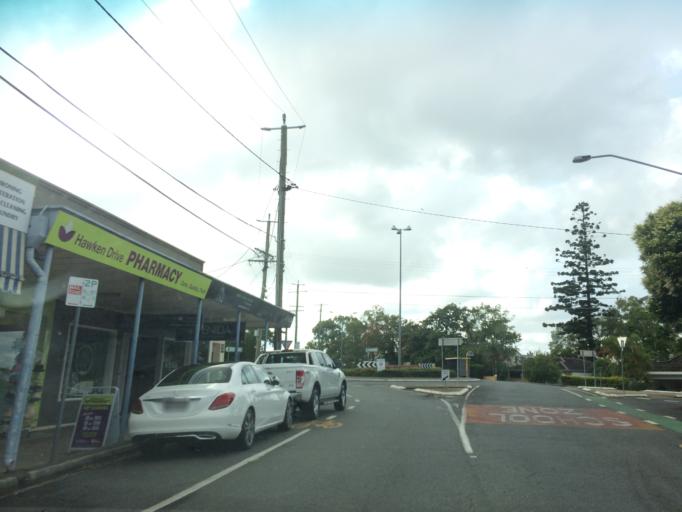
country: AU
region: Queensland
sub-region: Brisbane
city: Toowong
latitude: -27.5016
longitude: 152.9964
